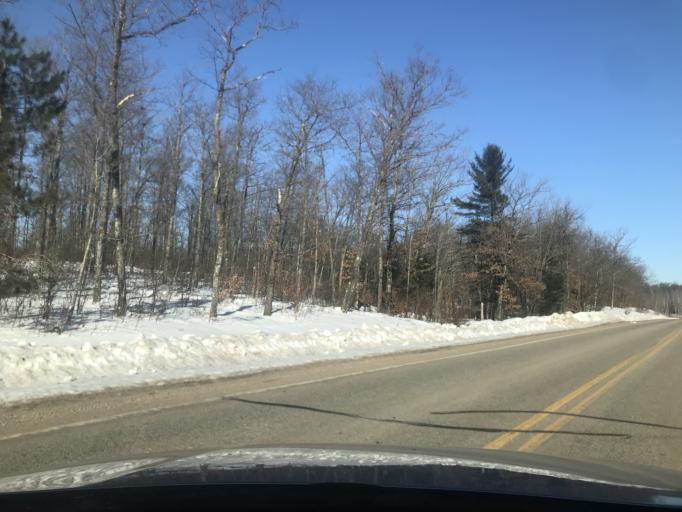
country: US
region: Wisconsin
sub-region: Marinette County
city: Niagara
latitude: 45.4228
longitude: -88.0214
